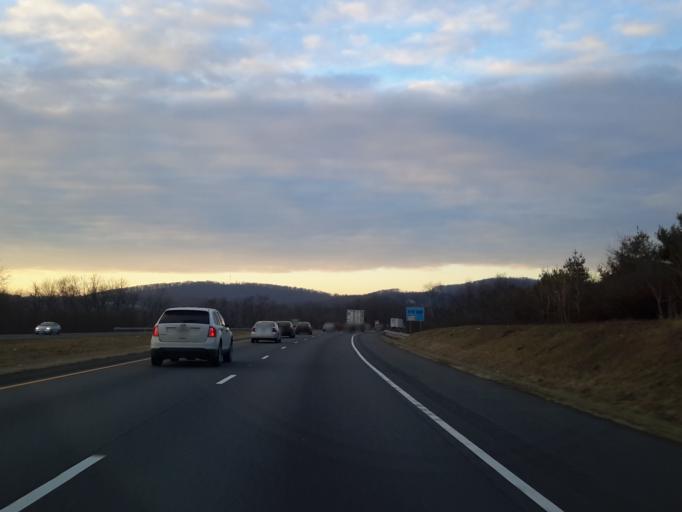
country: US
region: Maryland
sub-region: Frederick County
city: Braddock Heights
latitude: 39.4055
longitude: -77.4663
